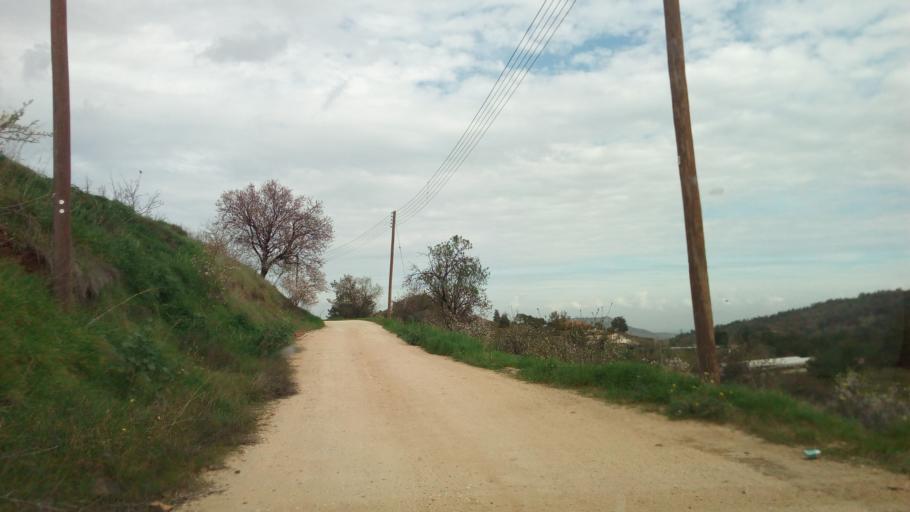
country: CY
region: Lefkosia
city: Klirou
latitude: 34.9986
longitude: 33.1146
